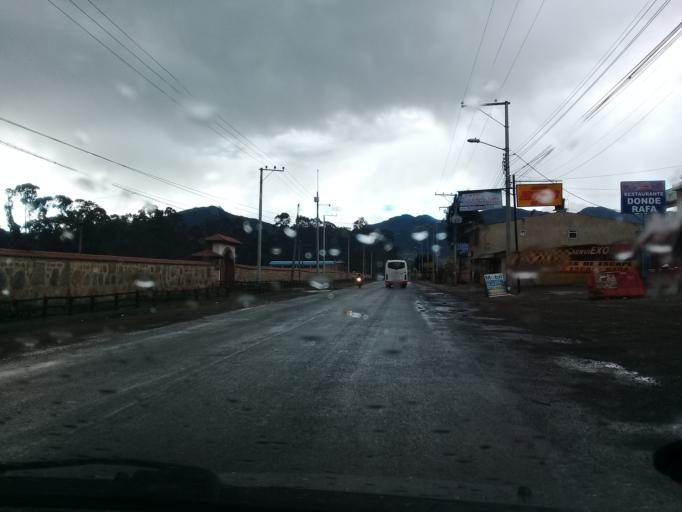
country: CO
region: Cundinamarca
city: Zipaquira
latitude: 5.0040
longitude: -73.9793
